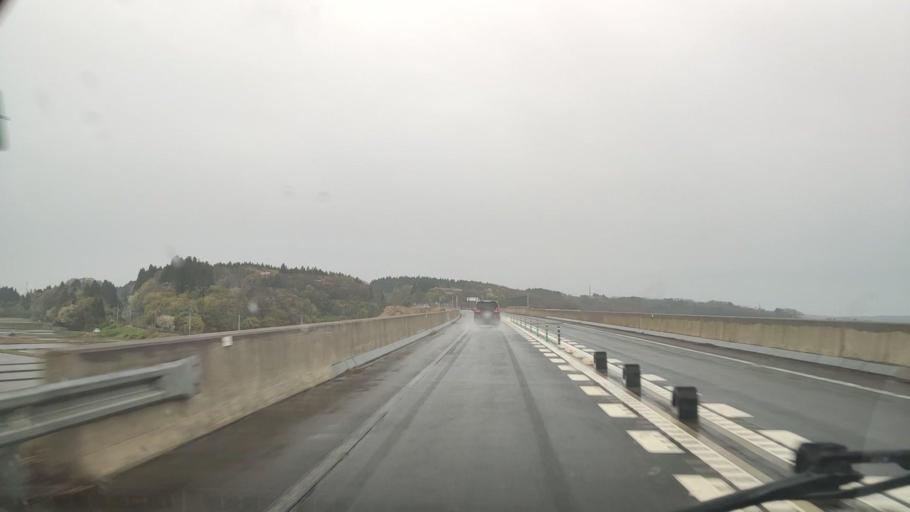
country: JP
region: Akita
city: Noshiromachi
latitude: 40.1787
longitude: 140.0600
